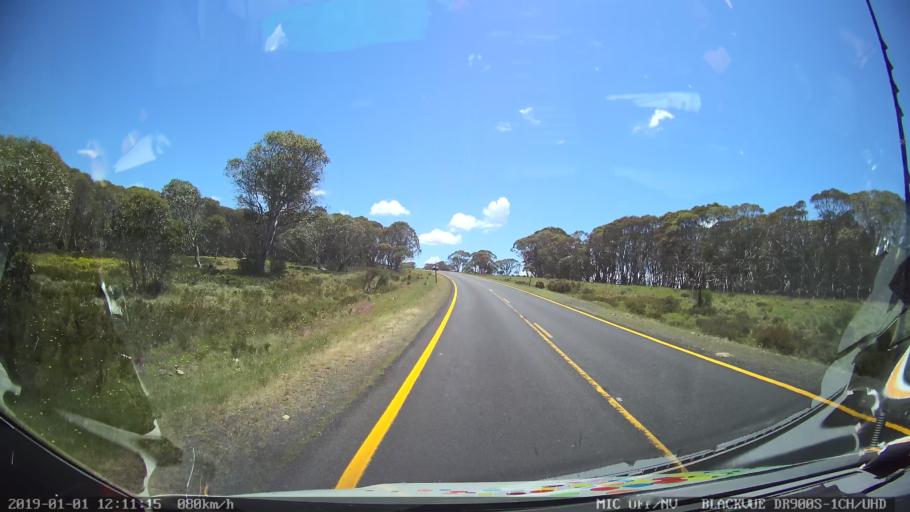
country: AU
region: New South Wales
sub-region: Tumut Shire
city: Tumut
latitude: -35.7862
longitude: 148.5071
